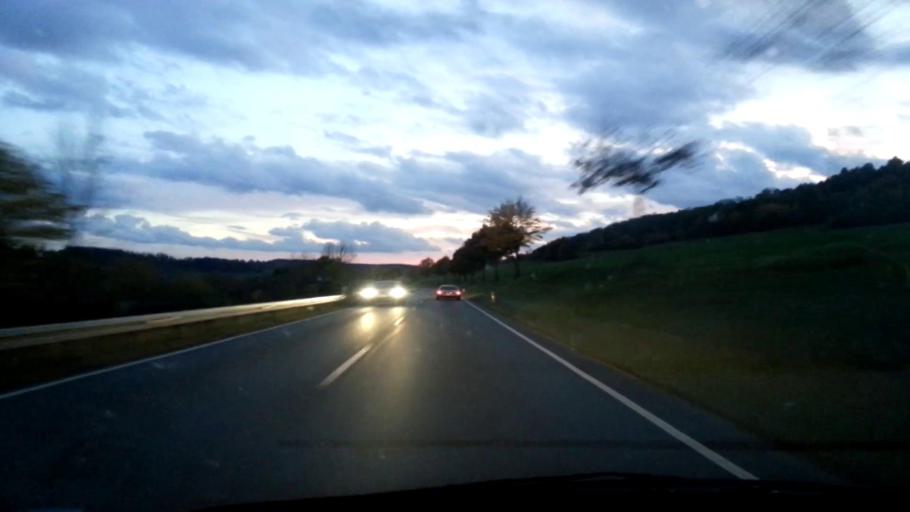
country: DE
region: Bavaria
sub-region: Upper Franconia
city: Reuth
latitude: 49.9699
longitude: 11.6662
